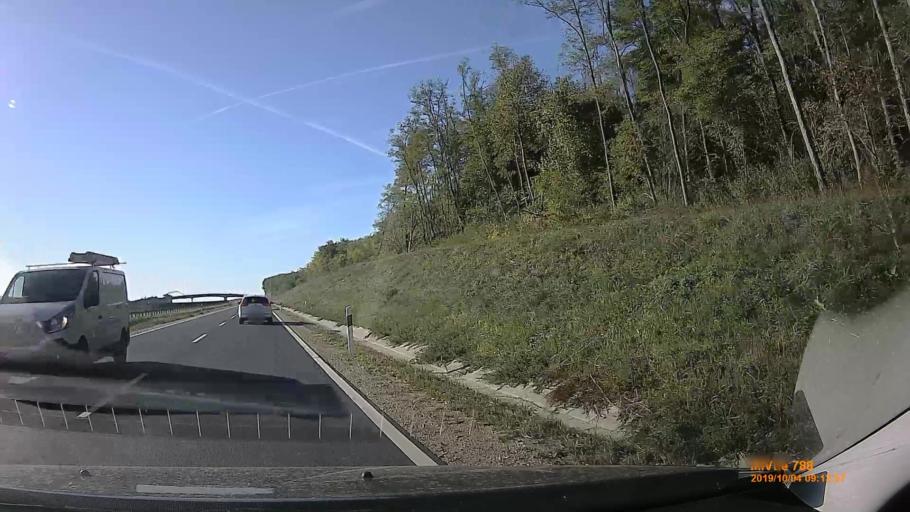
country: HU
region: Somogy
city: Karad
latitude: 46.6421
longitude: 17.7871
